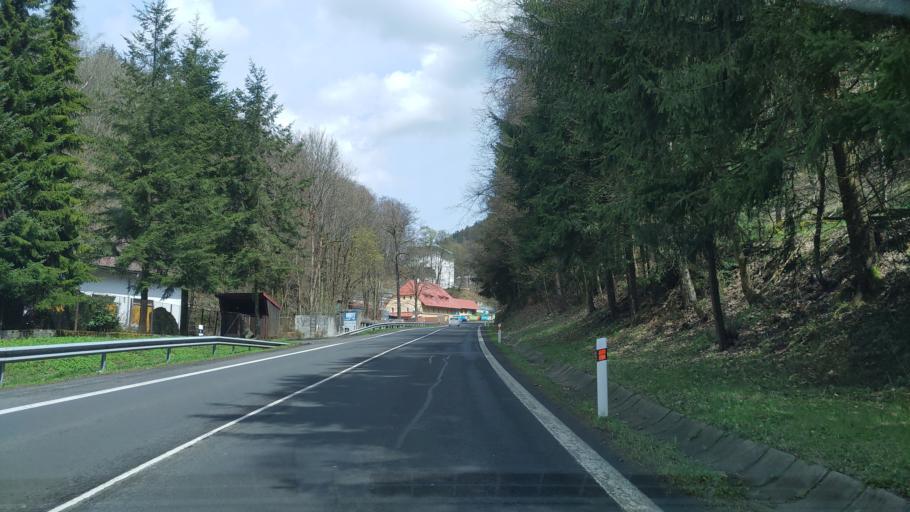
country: CZ
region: Karlovarsky
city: Jachymov
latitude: 50.3548
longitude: 12.9326
